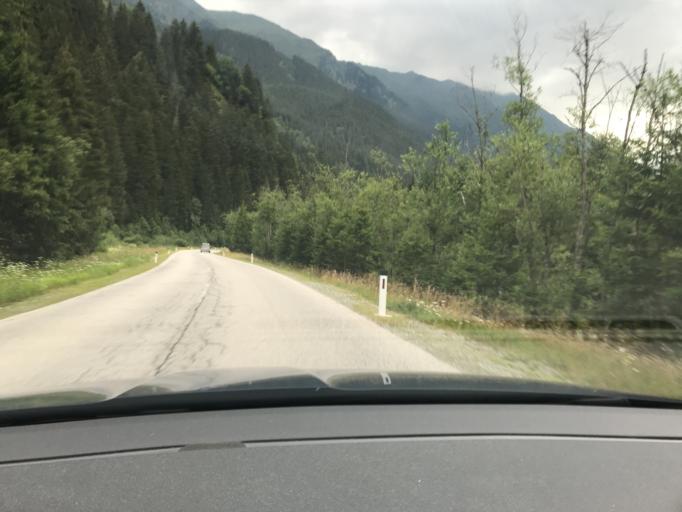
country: AT
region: Tyrol
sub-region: Politischer Bezirk Lienz
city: Virgen
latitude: 46.9228
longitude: 12.4377
